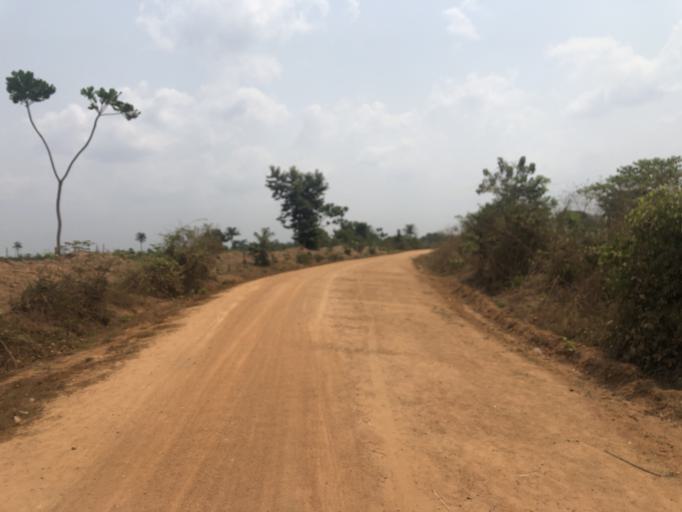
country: NG
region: Osun
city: Bode Osi
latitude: 7.7877
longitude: 4.1883
